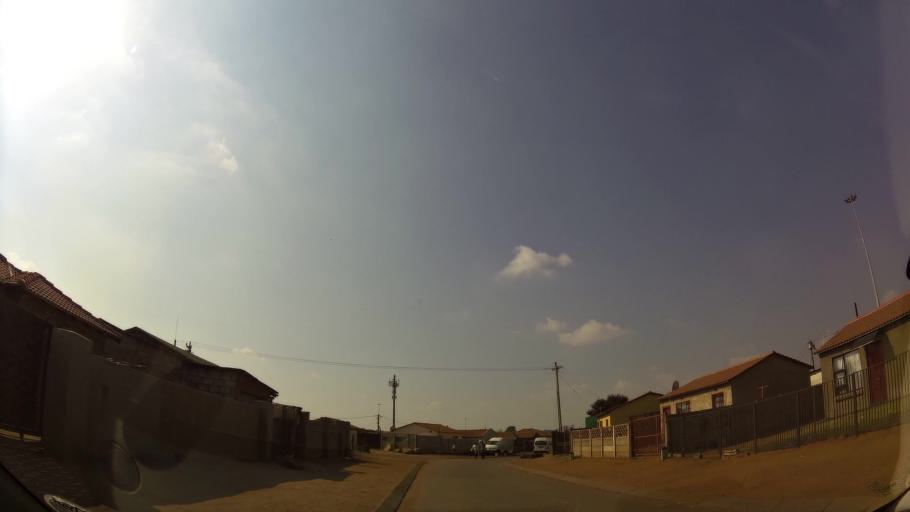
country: ZA
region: Gauteng
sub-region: Ekurhuleni Metropolitan Municipality
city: Springs
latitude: -26.1039
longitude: 28.4807
